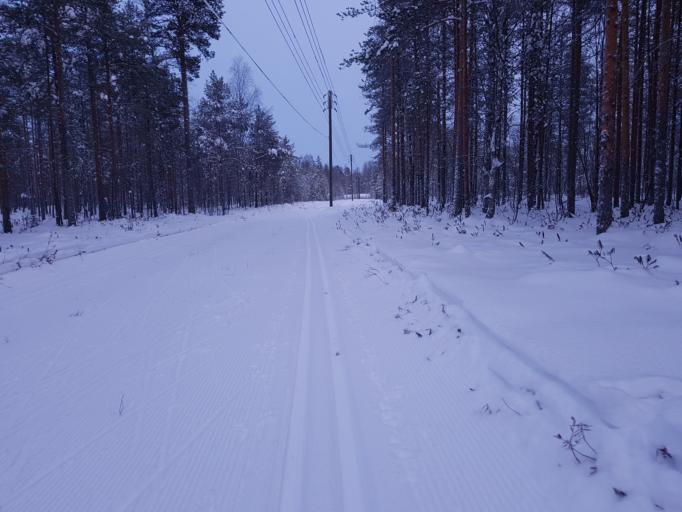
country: FI
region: Kainuu
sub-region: Kehys-Kainuu
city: Kuhmo
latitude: 64.1162
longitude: 29.5702
